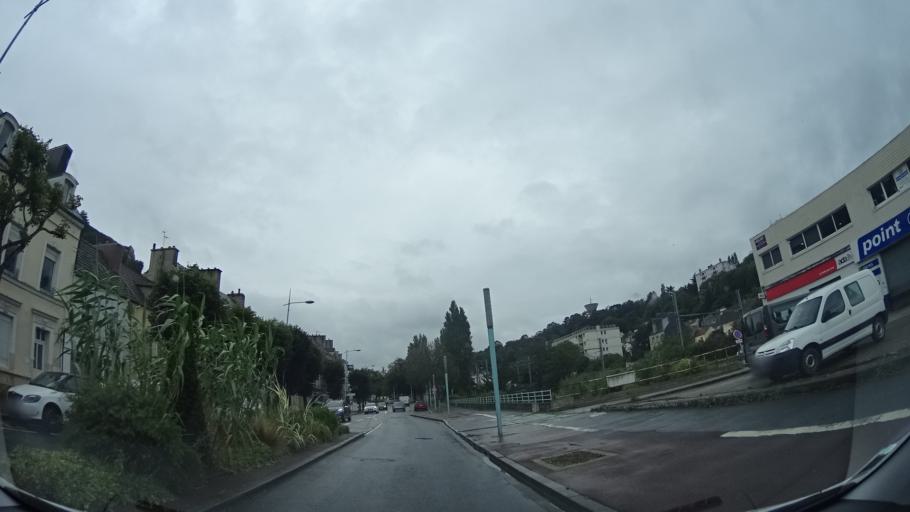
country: FR
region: Lower Normandy
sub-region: Departement de la Manche
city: Cherbourg-Octeville
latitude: 49.6295
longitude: -1.6181
